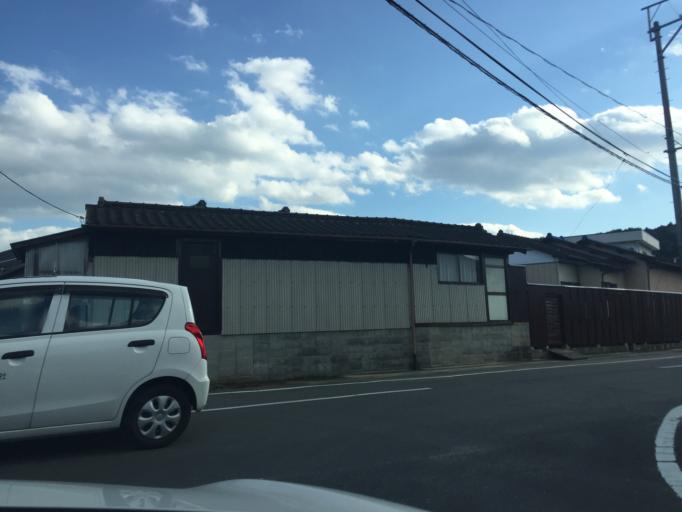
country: JP
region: Fukushima
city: Iwaki
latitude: 37.0604
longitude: 140.8634
